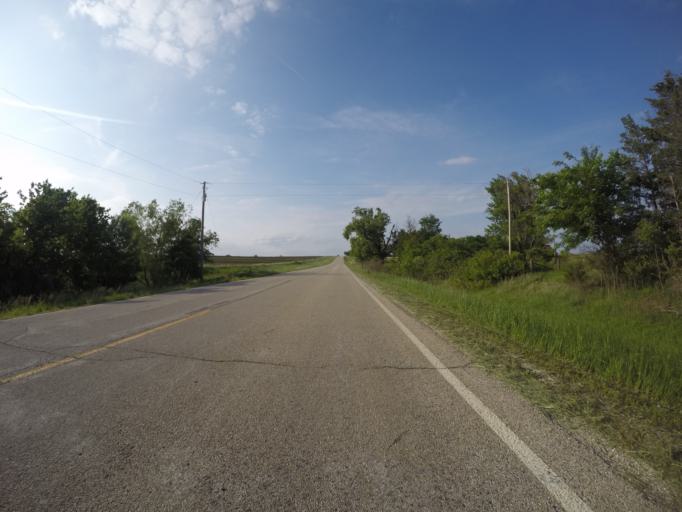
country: US
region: Kansas
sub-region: Pottawatomie County
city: Westmoreland
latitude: 39.4211
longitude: -96.6070
